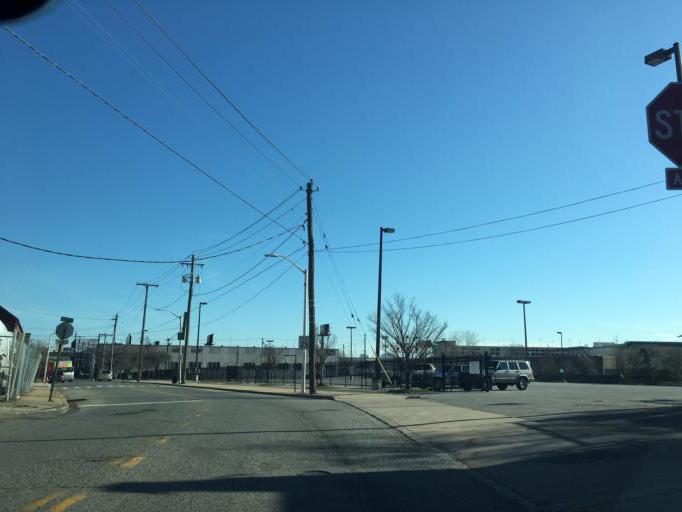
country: US
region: Maryland
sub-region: City of Baltimore
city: Baltimore
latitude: 39.2778
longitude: -76.6288
